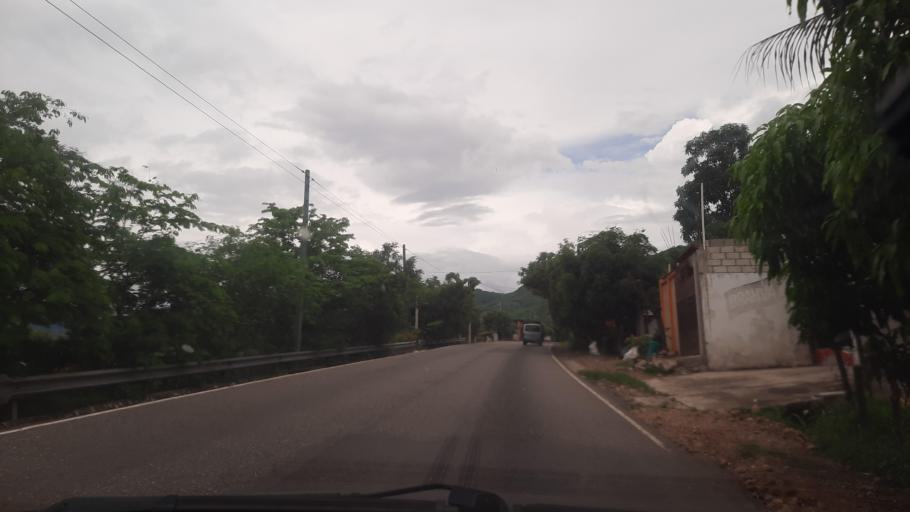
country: GT
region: Zacapa
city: San Jorge
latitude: 14.8994
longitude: -89.5219
